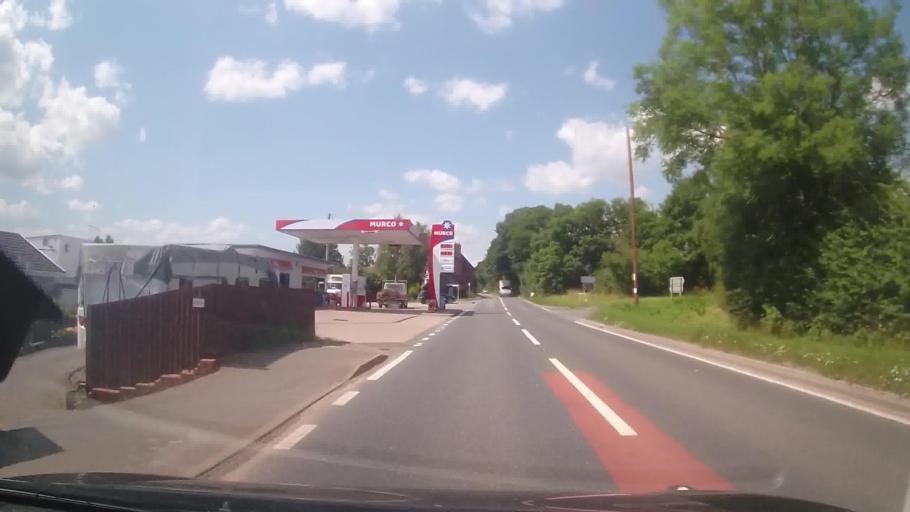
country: GB
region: England
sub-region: Herefordshire
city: Bodenham
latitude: 52.1611
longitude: -2.6725
